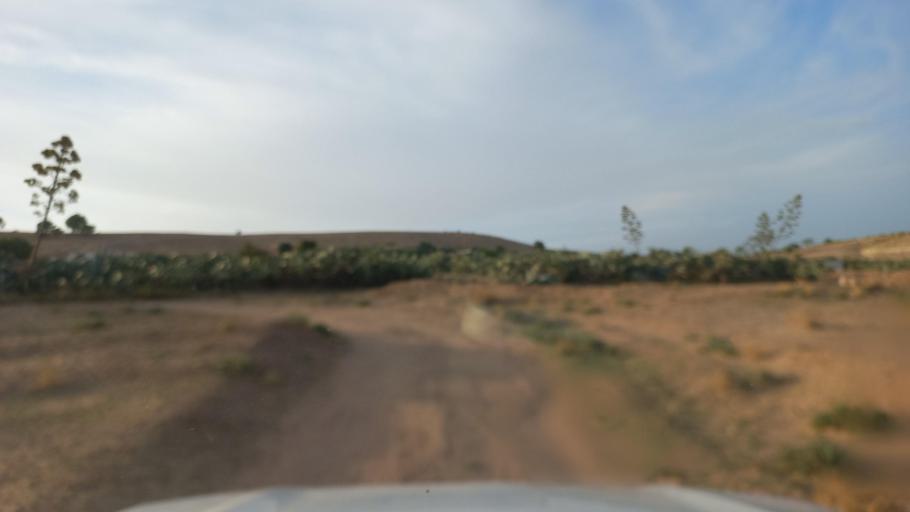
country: TN
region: Al Qasrayn
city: Sbiba
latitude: 35.4093
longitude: 8.9029
